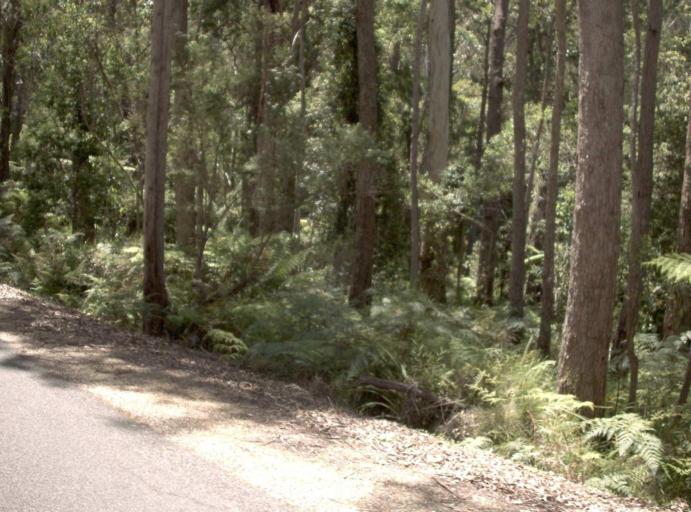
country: AU
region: New South Wales
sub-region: Bombala
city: Bombala
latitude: -37.4857
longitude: 148.9302
